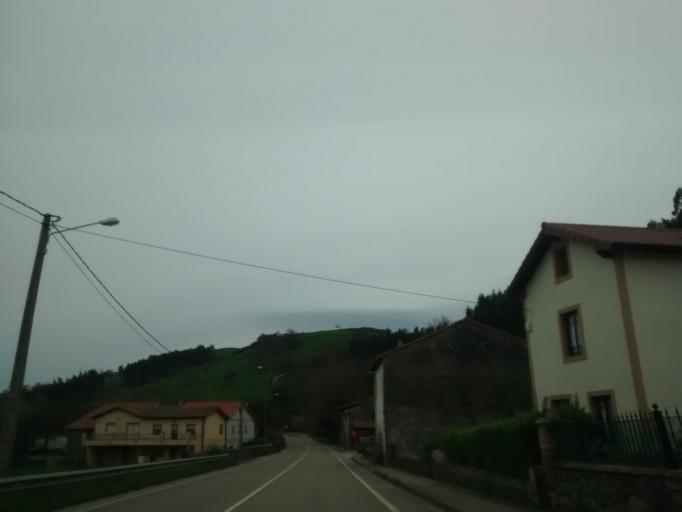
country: ES
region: Cantabria
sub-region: Provincia de Cantabria
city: Lierganes
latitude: 43.3540
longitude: -3.7629
